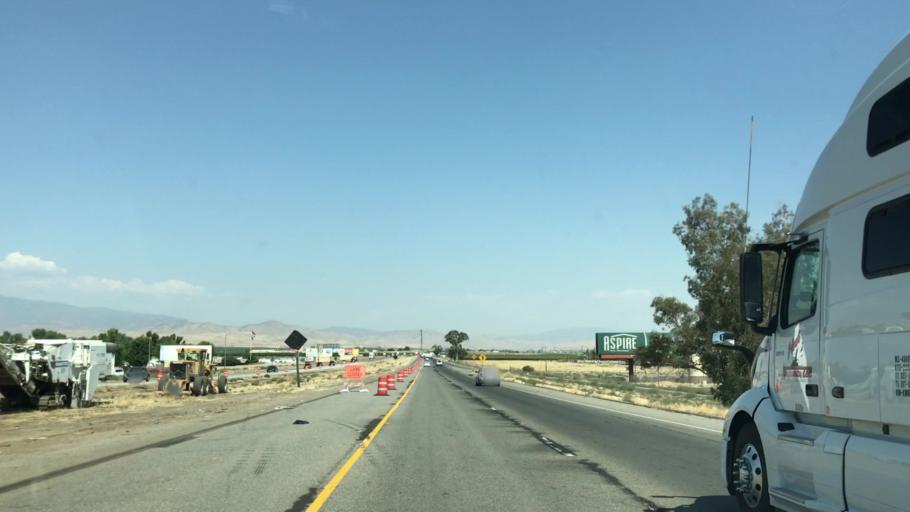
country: US
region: California
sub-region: Kern County
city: Lamont
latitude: 35.3521
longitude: -118.9128
